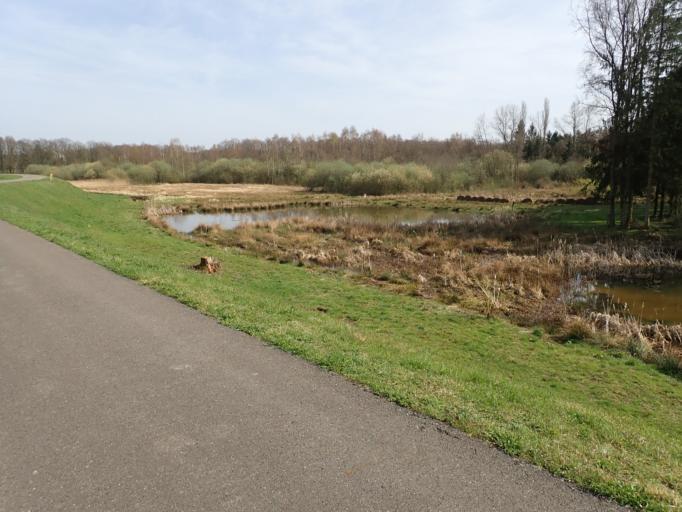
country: BE
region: Flanders
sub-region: Provincie Antwerpen
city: Lier
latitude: 51.1548
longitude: 4.6001
